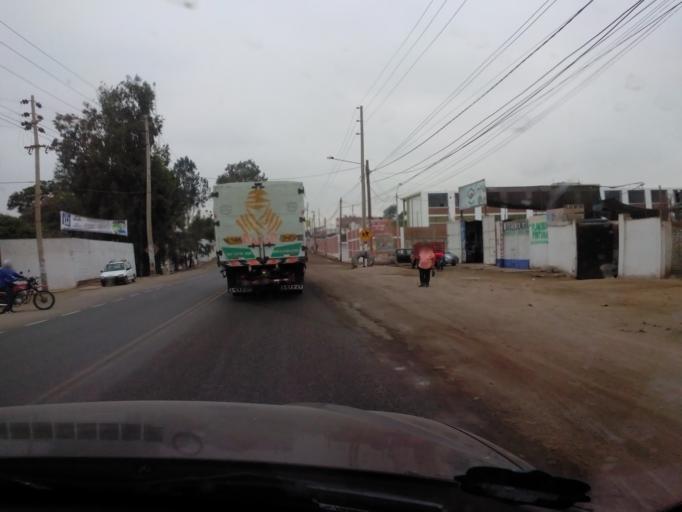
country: PE
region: Ica
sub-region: Provincia de Chincha
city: Chincha Baja
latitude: -13.4438
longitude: -76.1355
